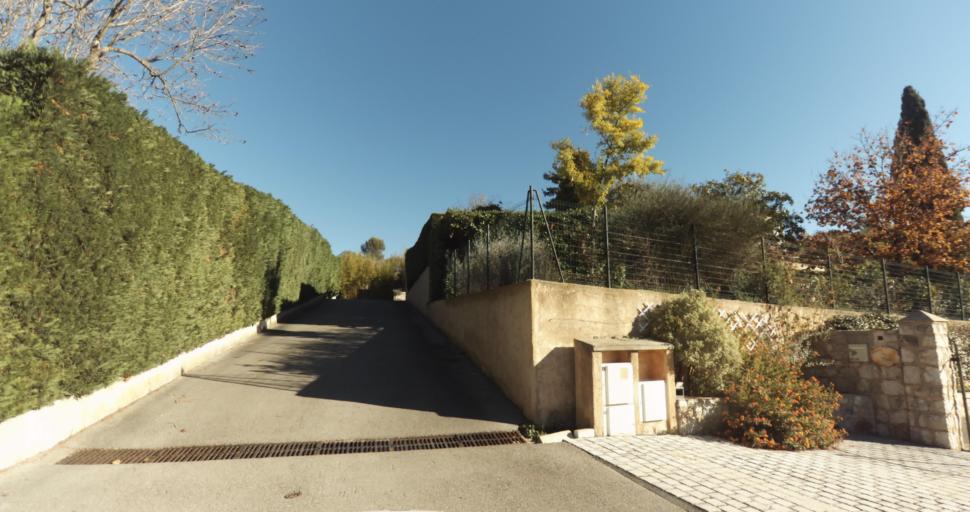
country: FR
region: Provence-Alpes-Cote d'Azur
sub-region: Departement des Alpes-Maritimes
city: Vence
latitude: 43.7178
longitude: 7.0911
